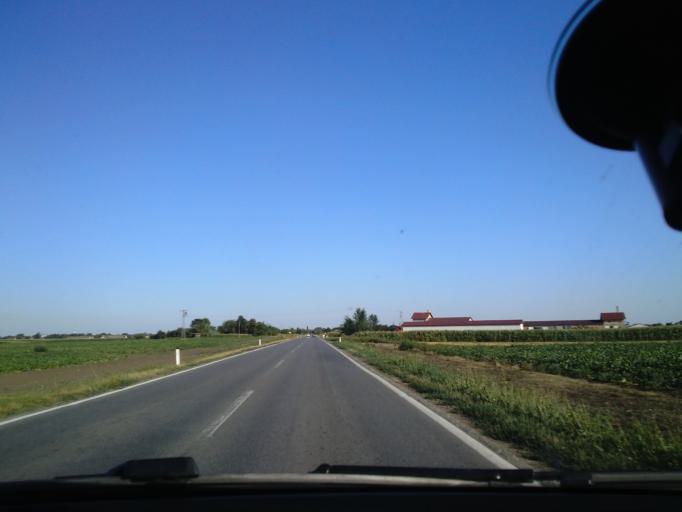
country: RS
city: Doroslovo
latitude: 45.6788
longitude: 19.1823
